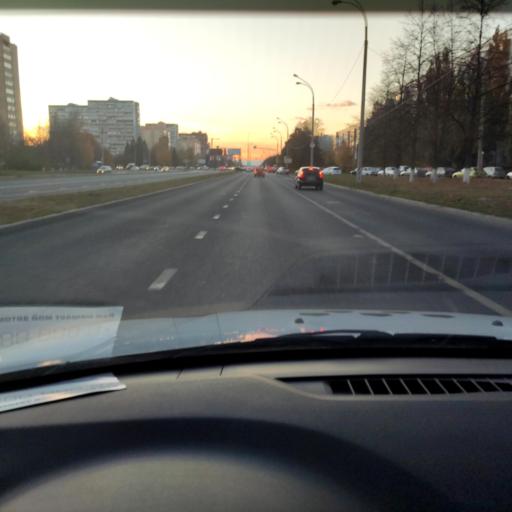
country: RU
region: Samara
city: Tol'yatti
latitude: 53.5260
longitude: 49.3158
